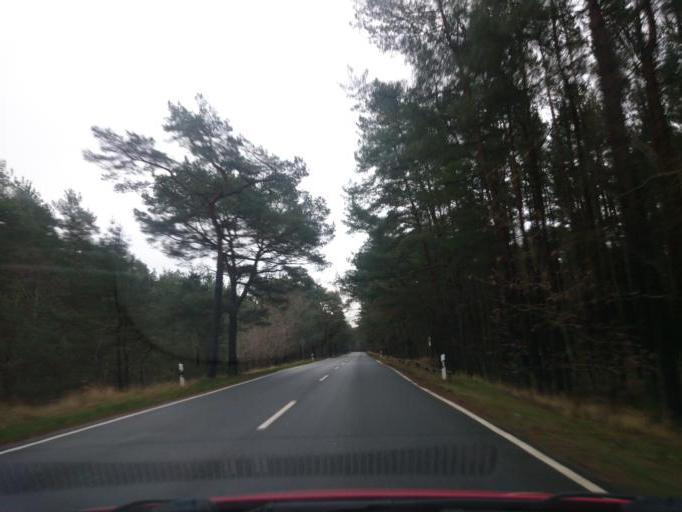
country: DE
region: Mecklenburg-Vorpommern
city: Glowe
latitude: 54.5778
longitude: 13.4135
